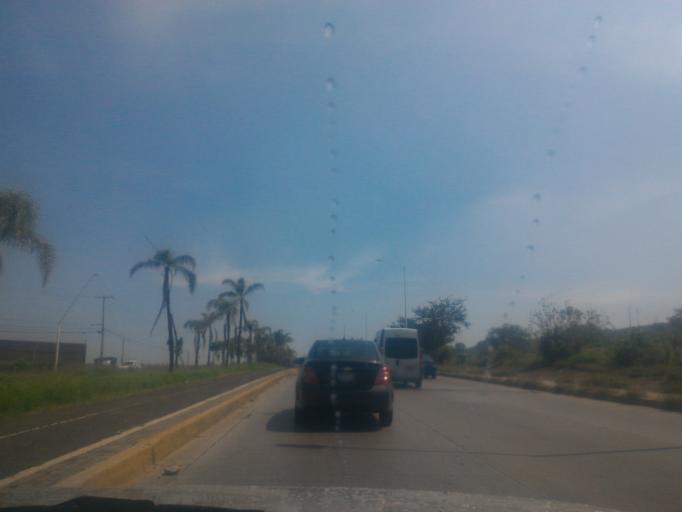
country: MX
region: Jalisco
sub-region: Tlajomulco de Zuniga
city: Altus Bosques
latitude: 20.5934
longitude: -103.3816
